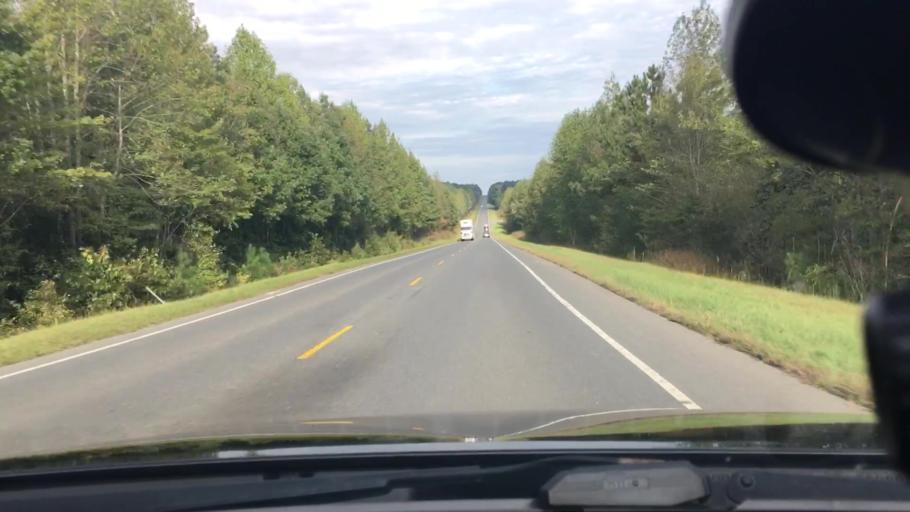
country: US
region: North Carolina
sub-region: Montgomery County
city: Mount Gilead
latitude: 35.3114
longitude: -79.9934
